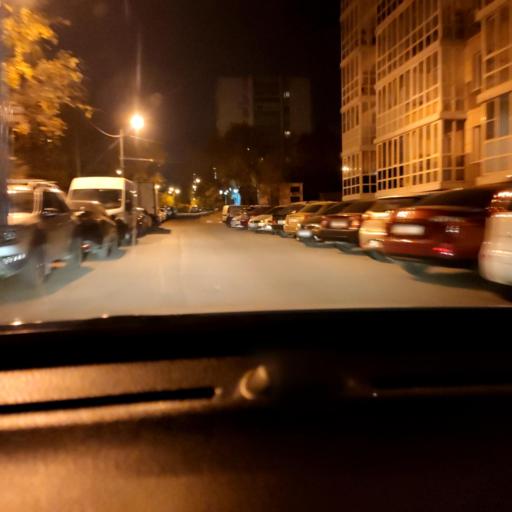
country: RU
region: Voronezj
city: Voronezh
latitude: 51.7129
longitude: 39.2711
